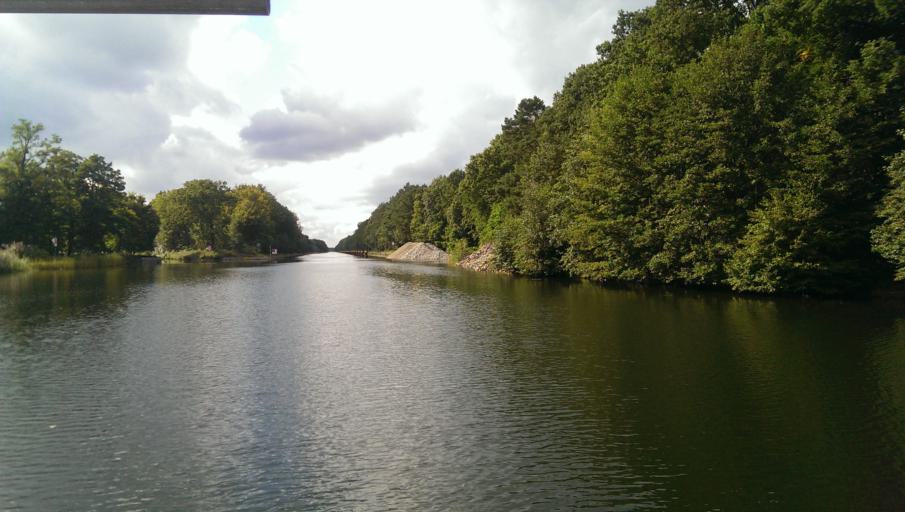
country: DE
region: Brandenburg
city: Marienwerder
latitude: 52.8511
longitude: 13.6071
